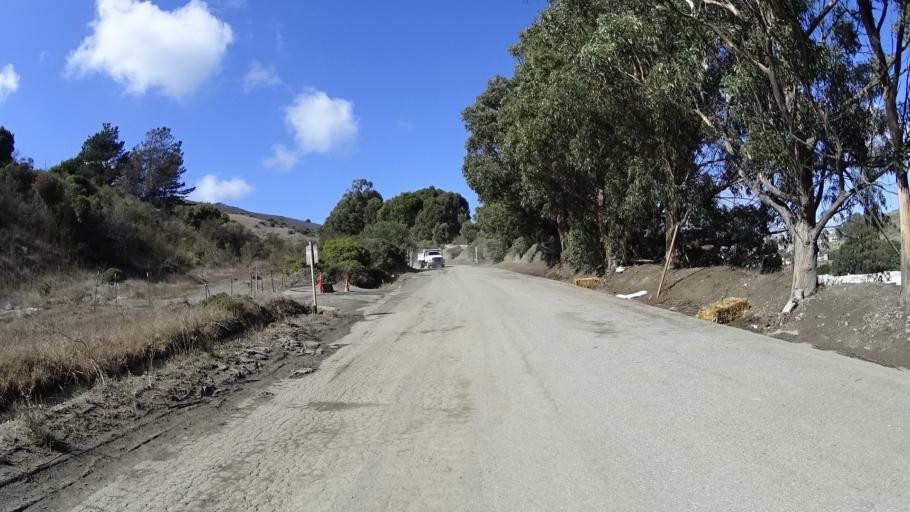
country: US
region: California
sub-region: San Mateo County
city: Brisbane
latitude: 37.6867
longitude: -122.4173
